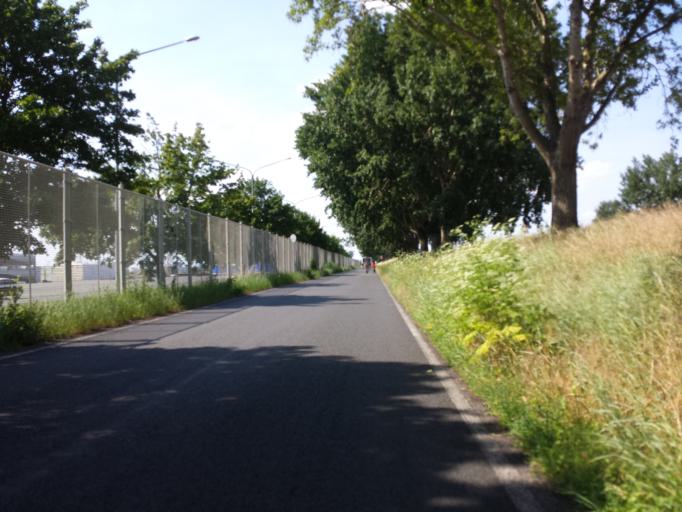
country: DE
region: Bremen
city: Bremen
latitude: 53.1029
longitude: 8.7464
